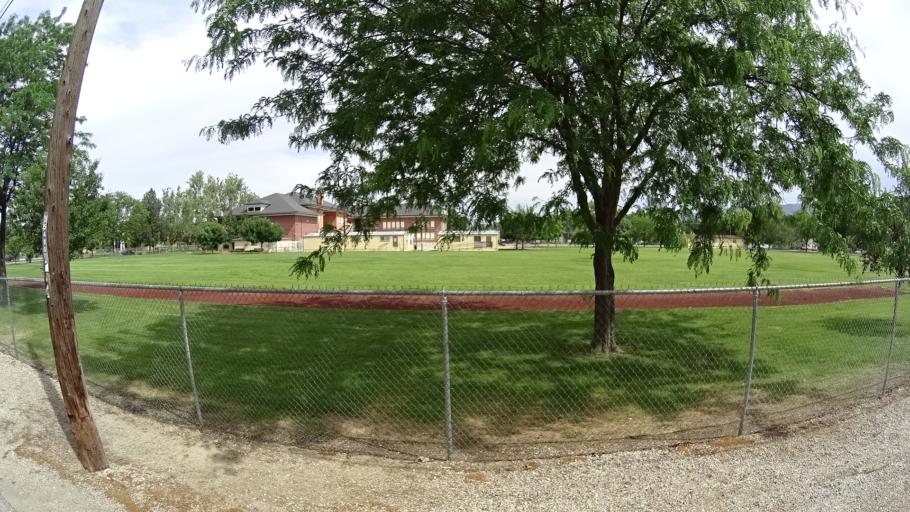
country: US
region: Idaho
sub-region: Ada County
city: Boise
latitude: 43.5880
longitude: -116.1923
